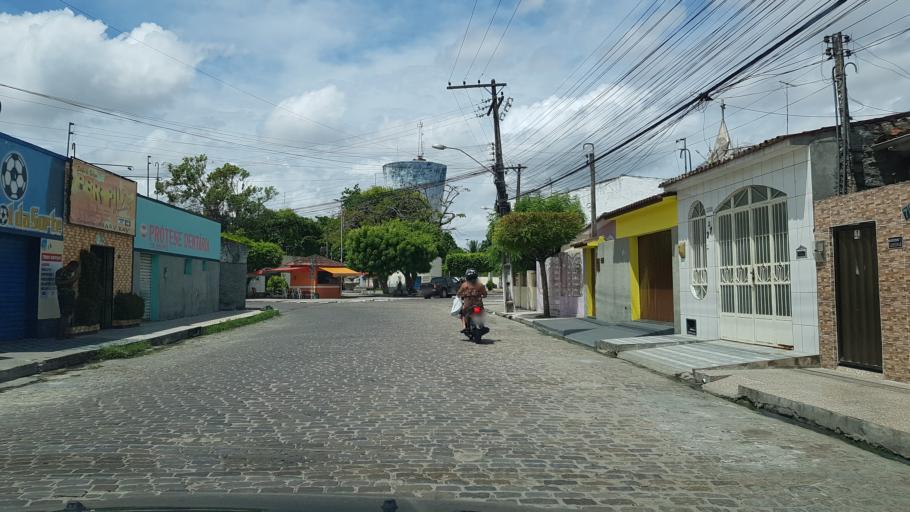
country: BR
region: Alagoas
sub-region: Penedo
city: Penedo
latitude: -10.2807
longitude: -36.5630
